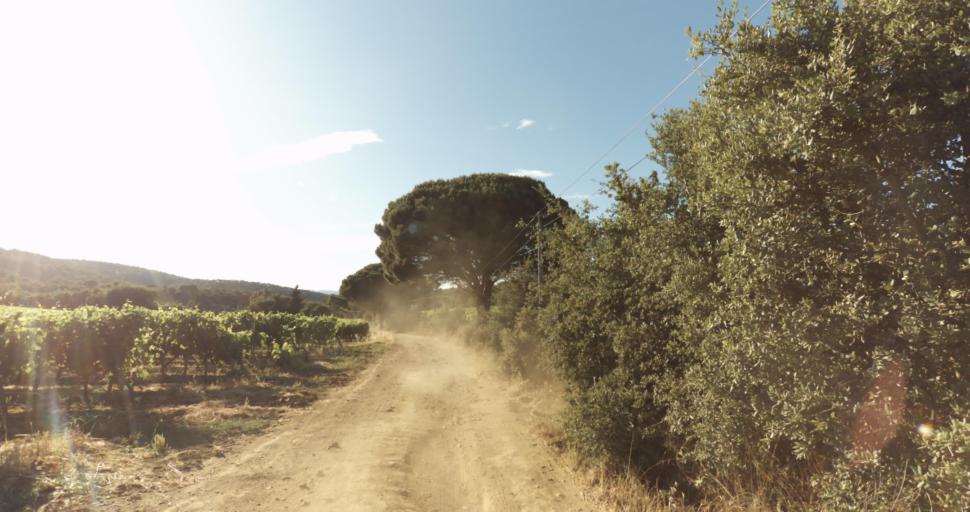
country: FR
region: Provence-Alpes-Cote d'Azur
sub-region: Departement du Var
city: La Croix-Valmer
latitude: 43.2199
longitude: 6.5628
